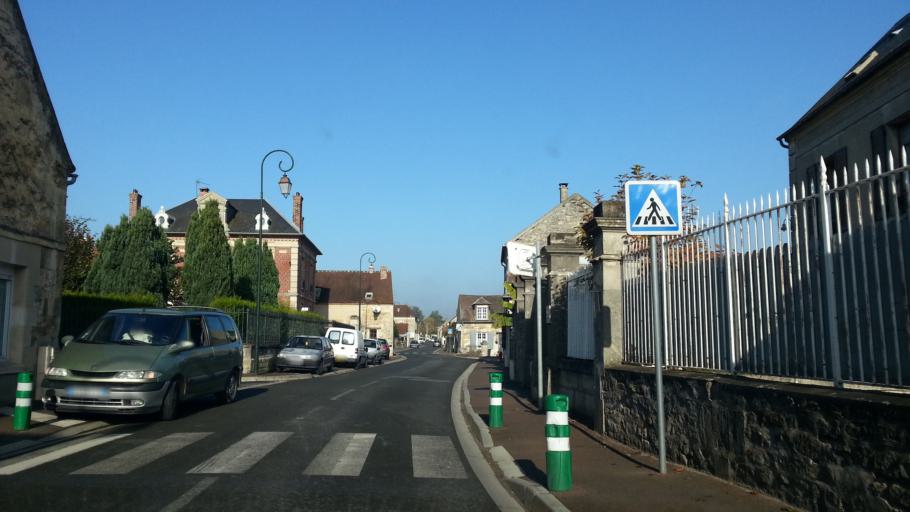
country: FR
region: Picardie
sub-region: Departement de l'Oise
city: Balagny-sur-Therain
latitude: 49.2976
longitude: 2.3341
